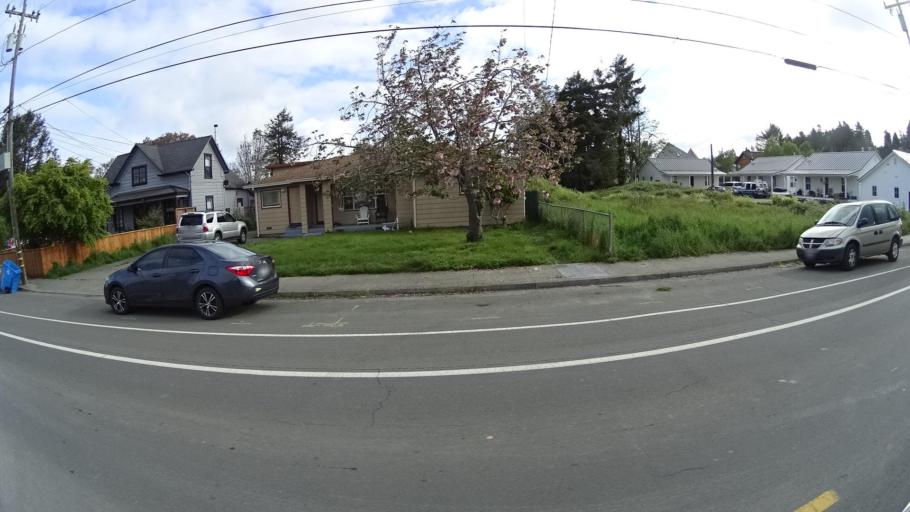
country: US
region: California
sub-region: Humboldt County
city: Arcata
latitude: 40.8893
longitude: -124.0843
